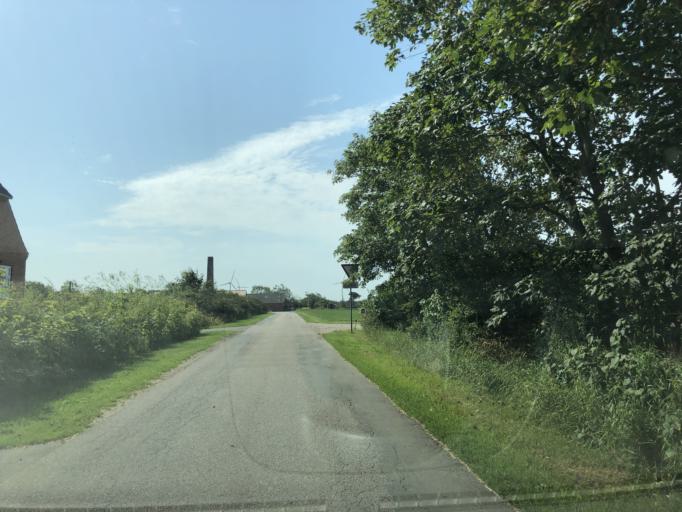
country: DK
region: Central Jutland
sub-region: Lemvig Kommune
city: Lemvig
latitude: 56.4245
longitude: 8.2611
